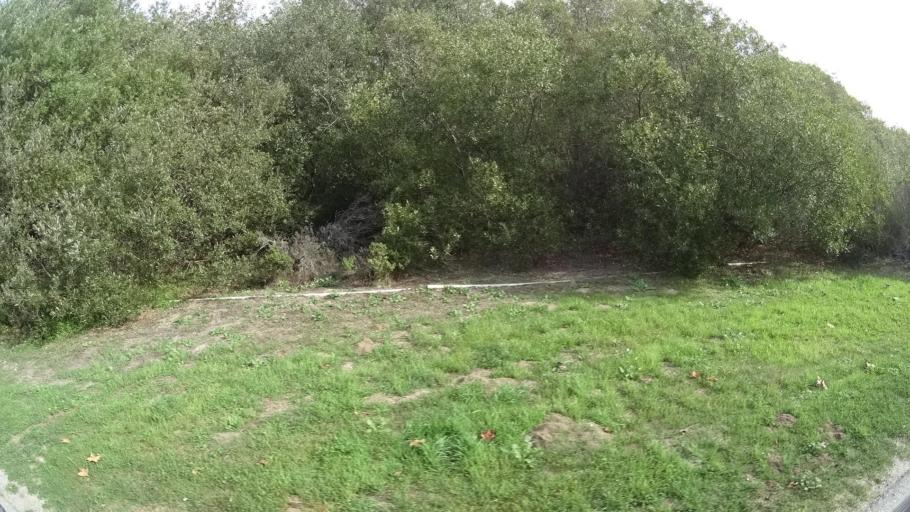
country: US
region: California
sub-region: Monterey County
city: Carmel-by-the-Sea
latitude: 36.5359
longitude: -121.9148
